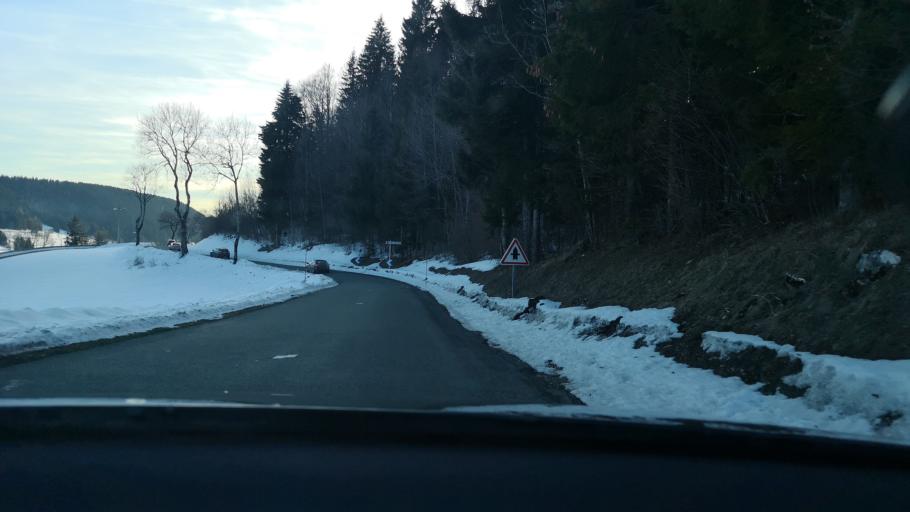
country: FR
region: Franche-Comte
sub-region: Departement du Doubs
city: La Cluse-et-Mijoux
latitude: 46.9457
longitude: 6.4381
